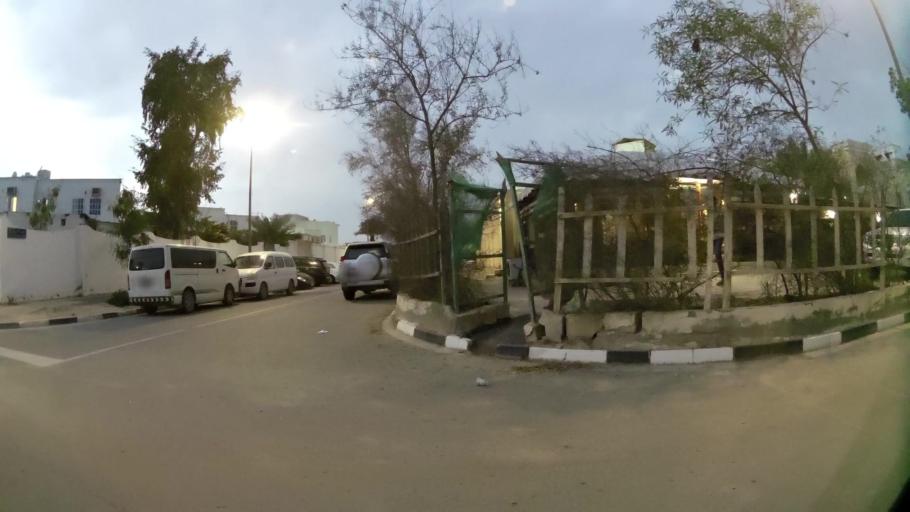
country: QA
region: Baladiyat ad Dawhah
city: Doha
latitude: 25.3442
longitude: 51.5113
